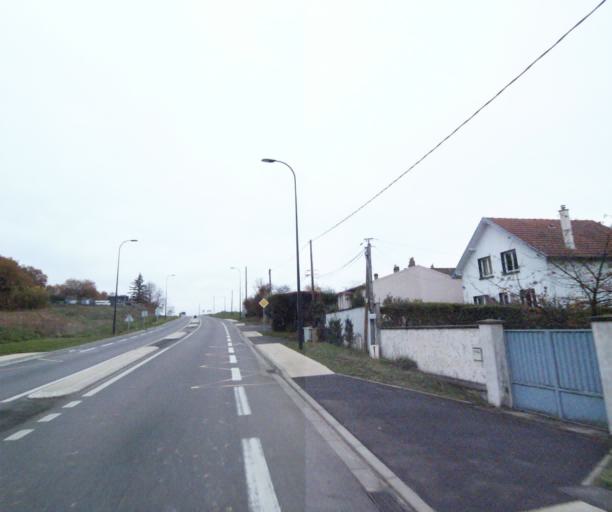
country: FR
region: Ile-de-France
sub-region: Departement des Yvelines
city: Villennes-sur-Seine
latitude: 48.9410
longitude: 1.9780
